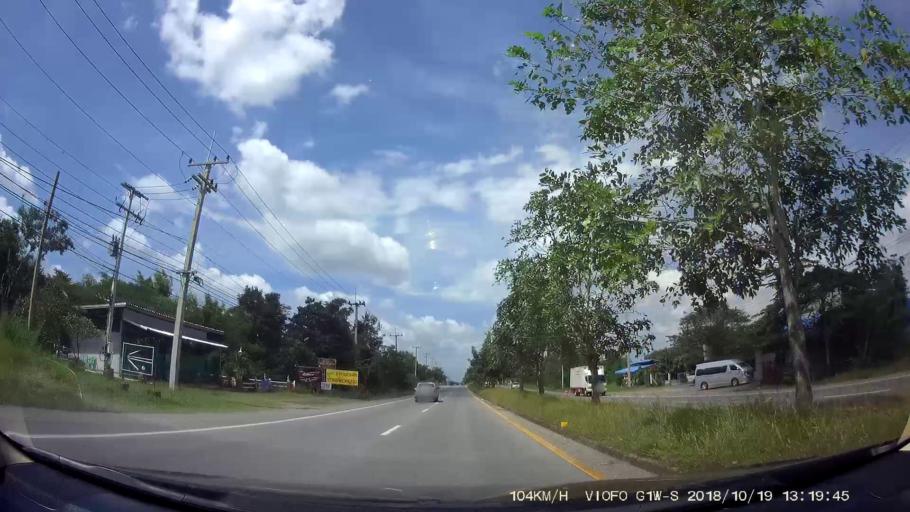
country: TH
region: Chaiyaphum
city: Chatturat
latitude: 15.4349
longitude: 101.8303
